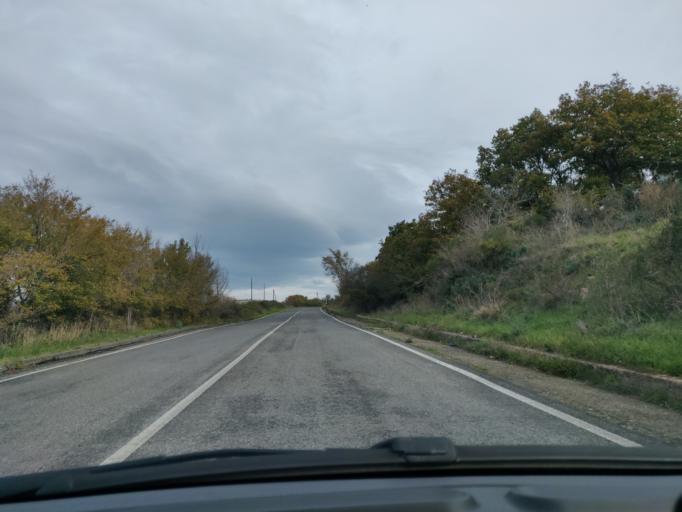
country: IT
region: Latium
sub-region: Citta metropolitana di Roma Capitale
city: Civitavecchia
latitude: 42.1129
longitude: 11.8533
